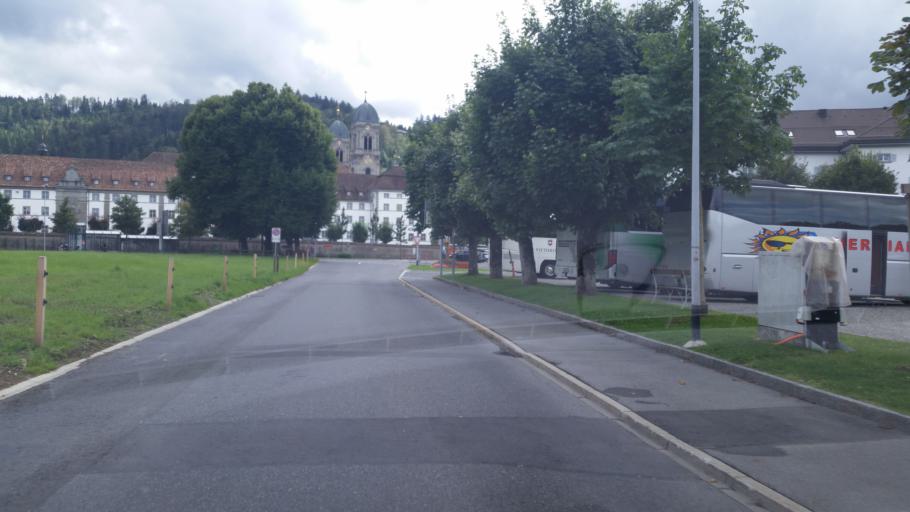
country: CH
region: Schwyz
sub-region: Bezirk Einsiedeln
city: Einsiedeln
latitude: 47.1291
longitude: 8.7520
